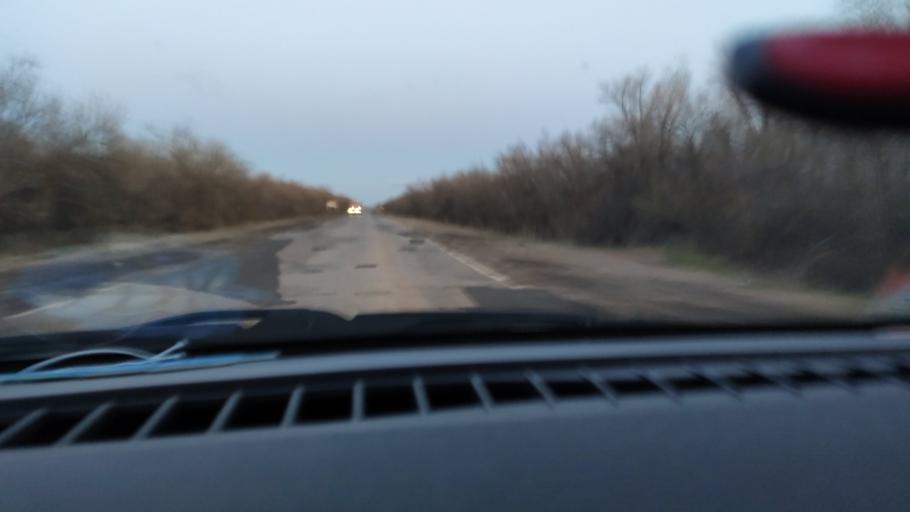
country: RU
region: Saratov
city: Krasnoarmeysk
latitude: 51.0755
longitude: 45.9775
